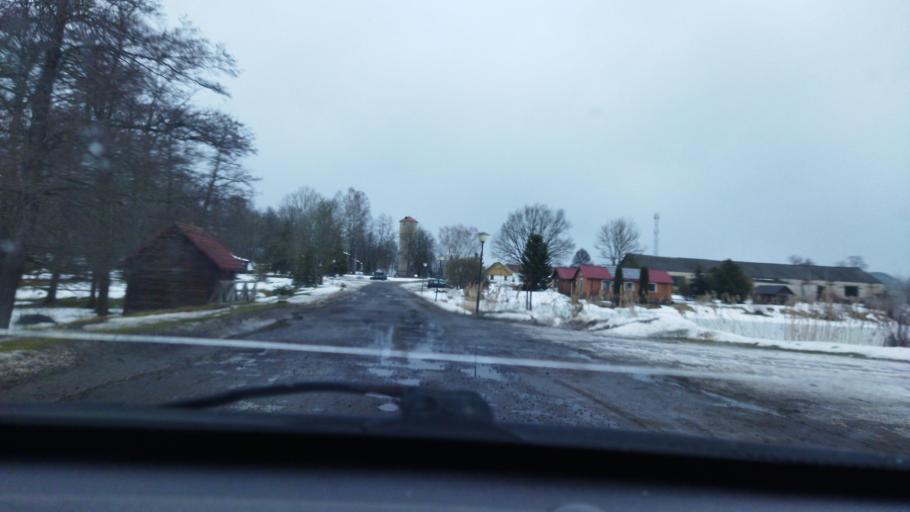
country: BY
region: Minsk
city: Svir
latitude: 54.9005
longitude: 26.4011
